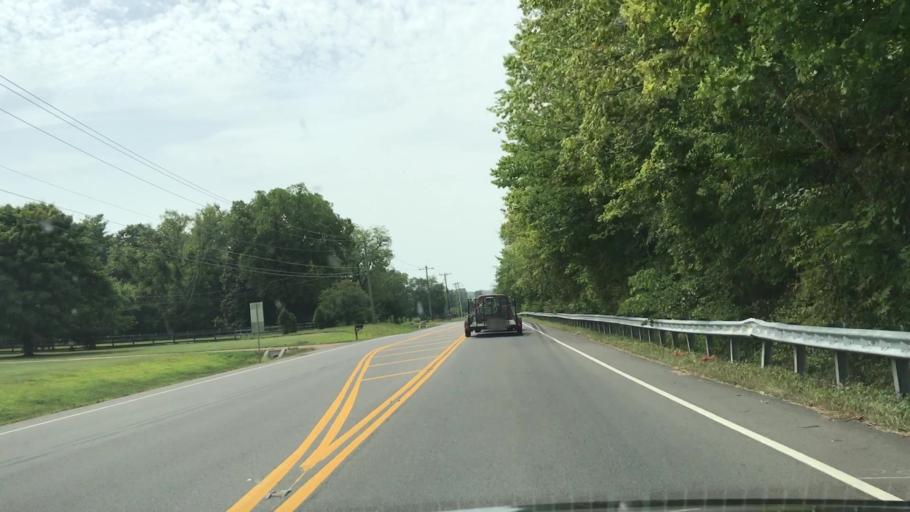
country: US
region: Tennessee
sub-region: Williamson County
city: Brentwood Estates
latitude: 35.9367
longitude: -86.7681
